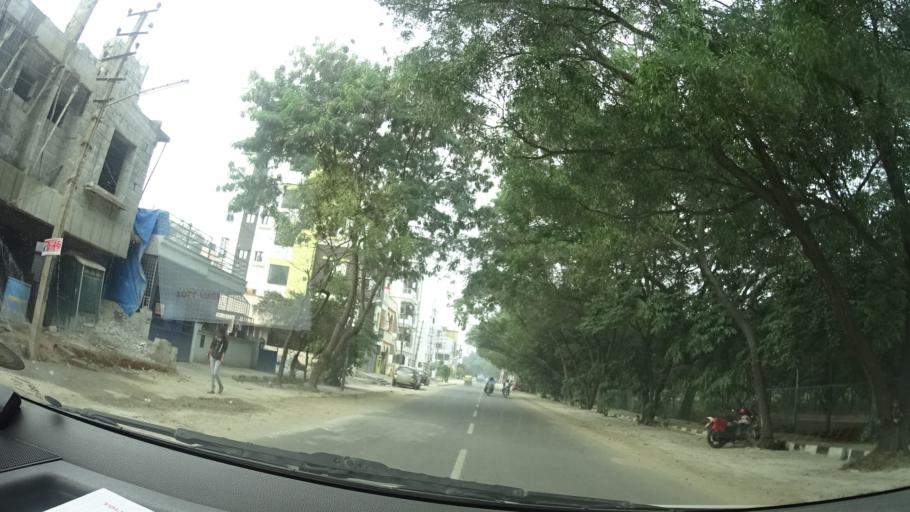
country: IN
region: Karnataka
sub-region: Bangalore Urban
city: Bangalore
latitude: 13.0329
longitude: 77.6270
